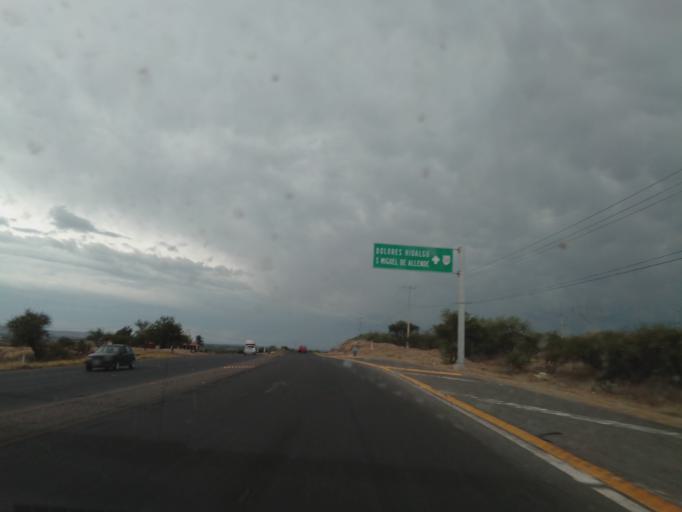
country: MX
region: Guanajuato
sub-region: Dolores Hidalgo Cuna de la Independencia Nacional
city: Ejido Jesus Maria
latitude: 21.1751
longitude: -100.8847
